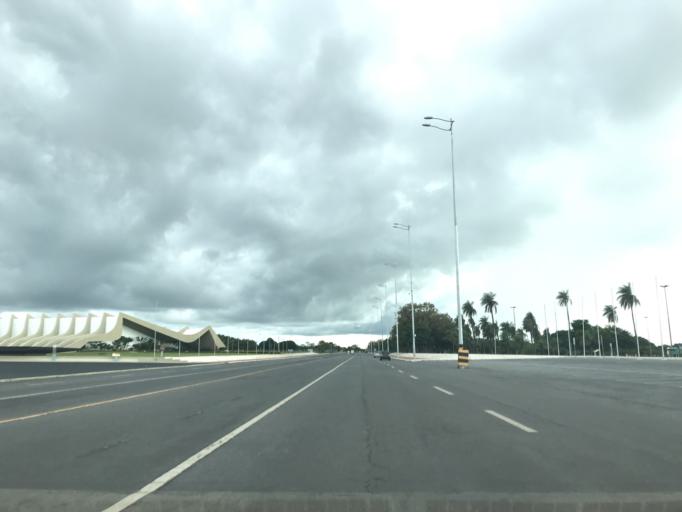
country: BR
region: Federal District
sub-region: Brasilia
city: Brasilia
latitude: -15.7727
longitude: -47.9199
